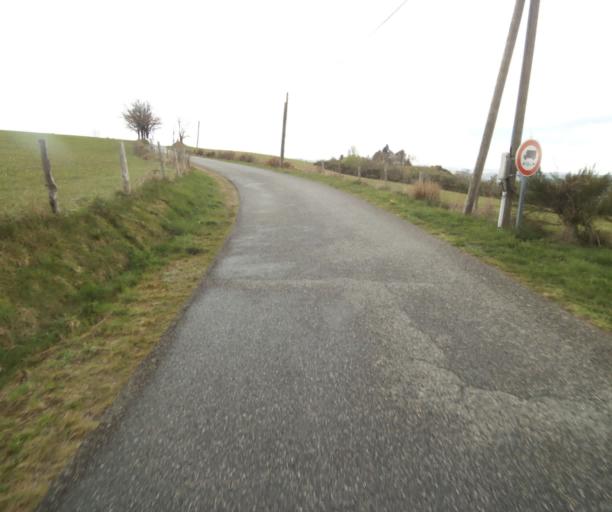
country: FR
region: Limousin
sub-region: Departement de la Correze
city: Naves
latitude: 45.3060
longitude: 1.8181
